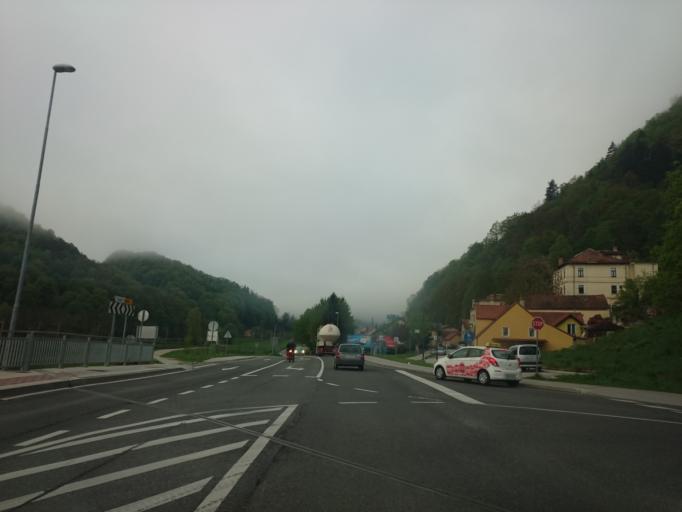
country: SI
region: Celje
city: Celje
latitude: 46.2246
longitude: 15.2663
